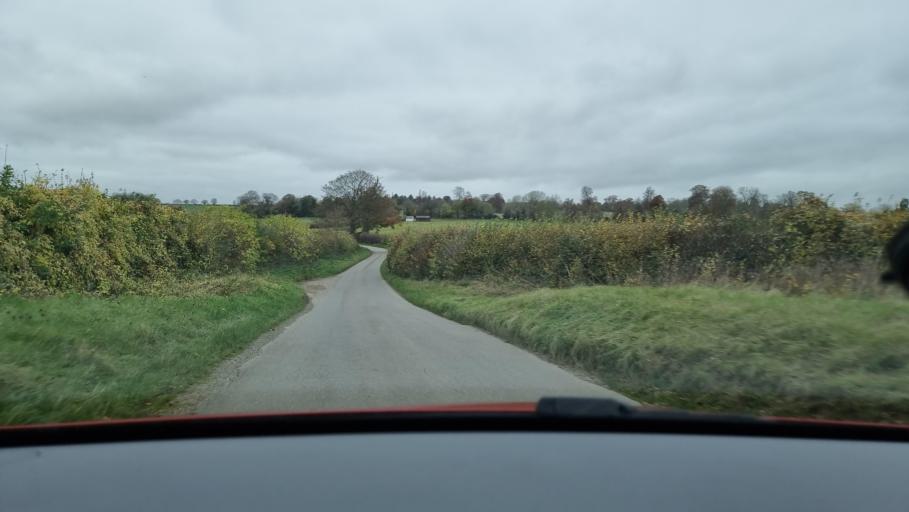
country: GB
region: England
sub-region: Oxfordshire
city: Woodstock
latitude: 51.8706
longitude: -1.3064
